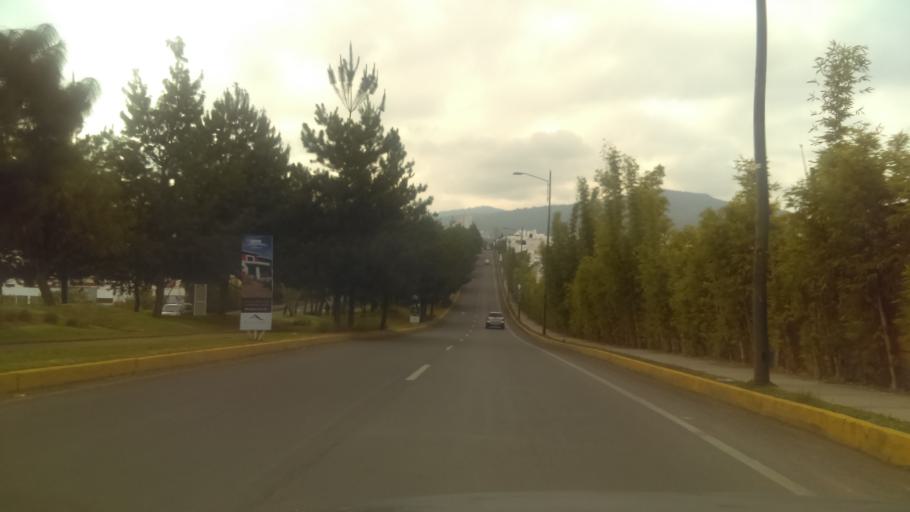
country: MX
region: Michoacan
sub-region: Morelia
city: Montana Monarca (Punta Altozano)
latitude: 19.6642
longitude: -101.1646
